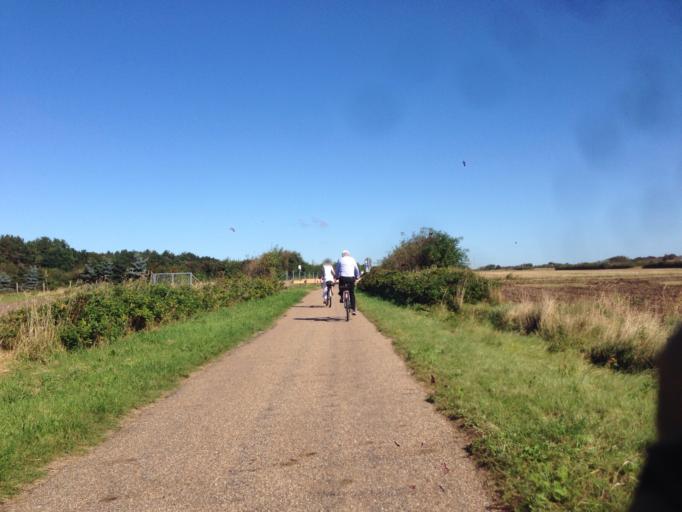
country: DE
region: Schleswig-Holstein
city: Tinnum
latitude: 54.9423
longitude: 8.3323
